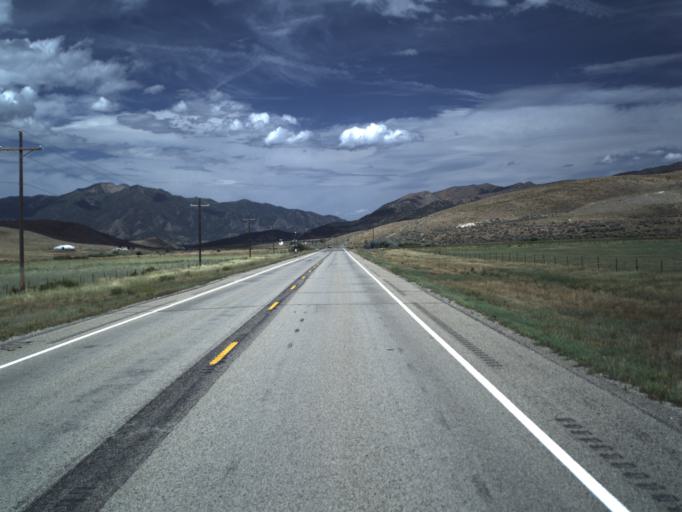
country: US
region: Utah
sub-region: Sanpete County
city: Fairview
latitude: 39.8097
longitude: -111.5050
